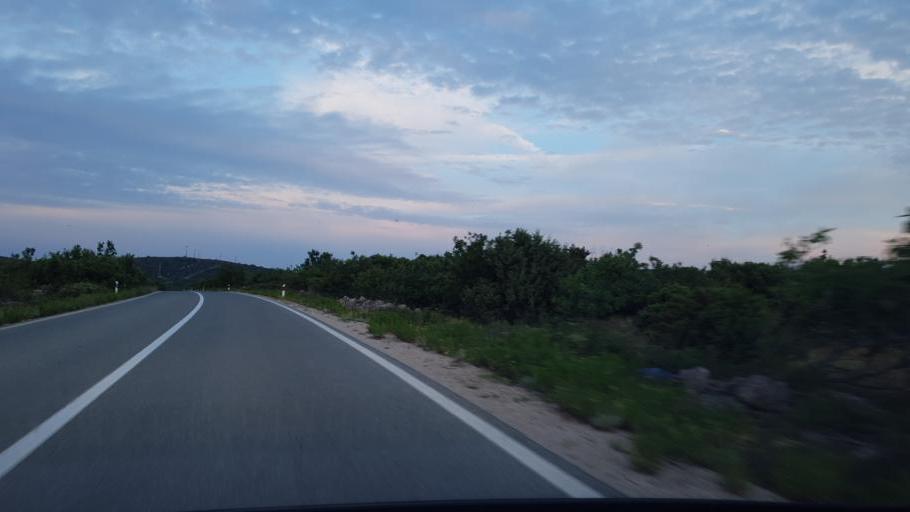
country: HR
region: Primorsko-Goranska
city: Punat
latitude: 45.0360
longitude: 14.6512
